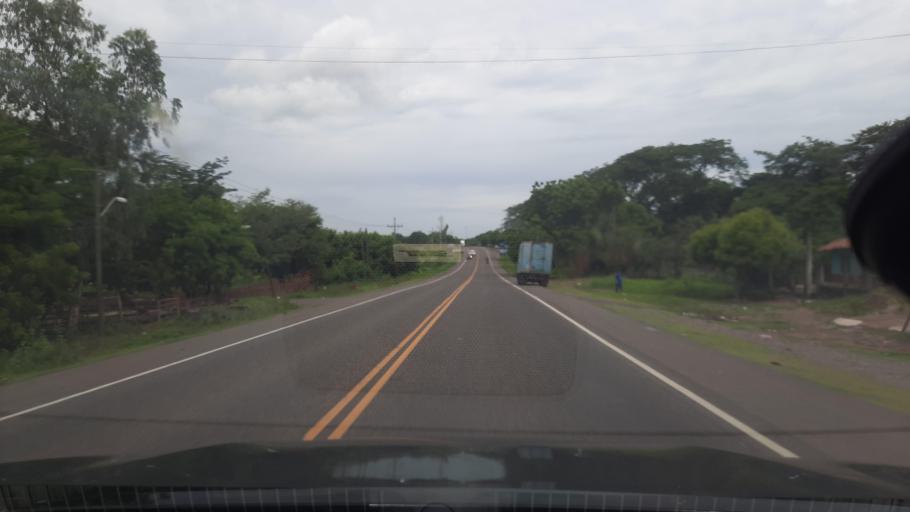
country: HN
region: Valle
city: Jicaro Galan
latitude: 13.5090
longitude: -87.4407
